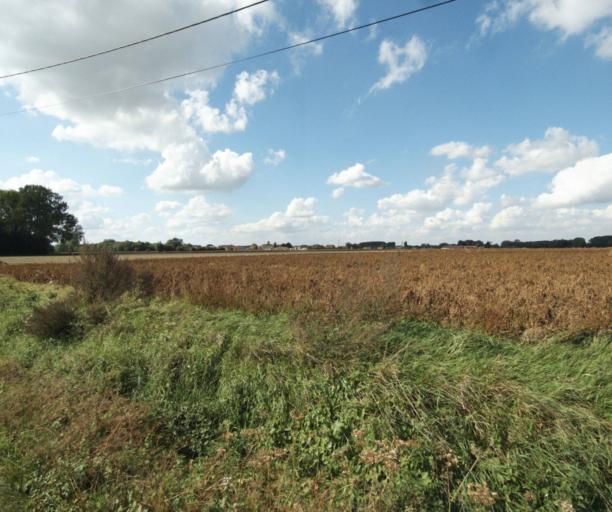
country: FR
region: Nord-Pas-de-Calais
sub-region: Departement du Nord
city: Illies
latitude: 50.5547
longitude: 2.8133
